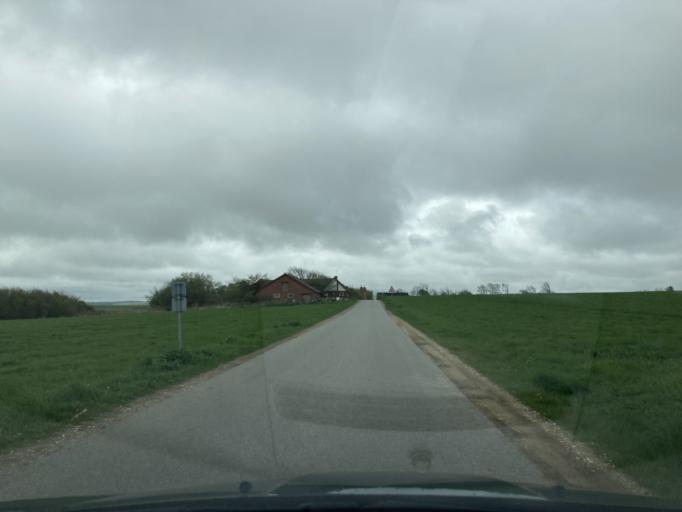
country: DK
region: North Denmark
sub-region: Thisted Kommune
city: Hurup
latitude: 56.8179
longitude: 8.3377
